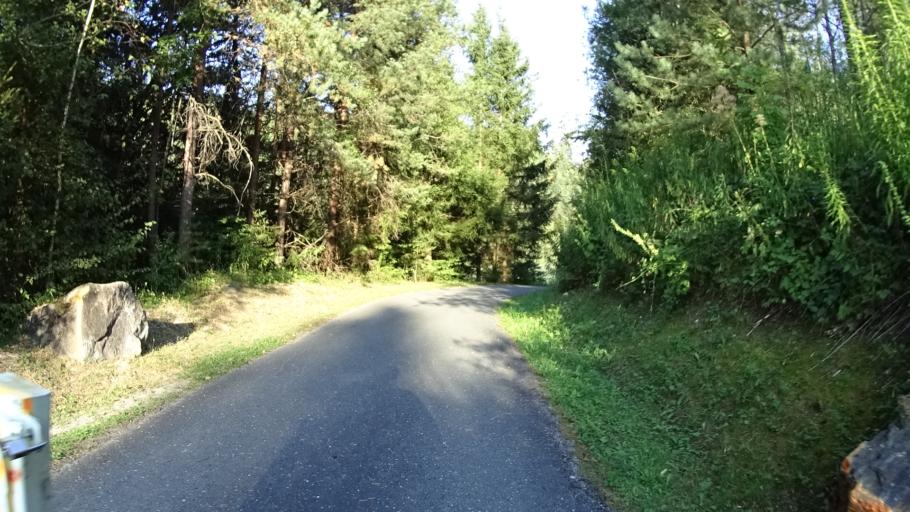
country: AT
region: Carinthia
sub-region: Politischer Bezirk Villach Land
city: Rosegg
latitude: 46.5800
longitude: 14.0173
